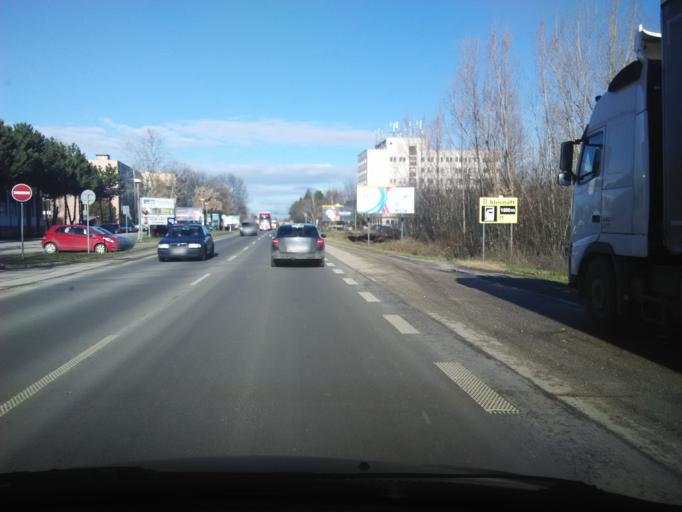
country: SK
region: Nitriansky
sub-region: Okres Nitra
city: Nitra
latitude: 48.2664
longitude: 18.1027
